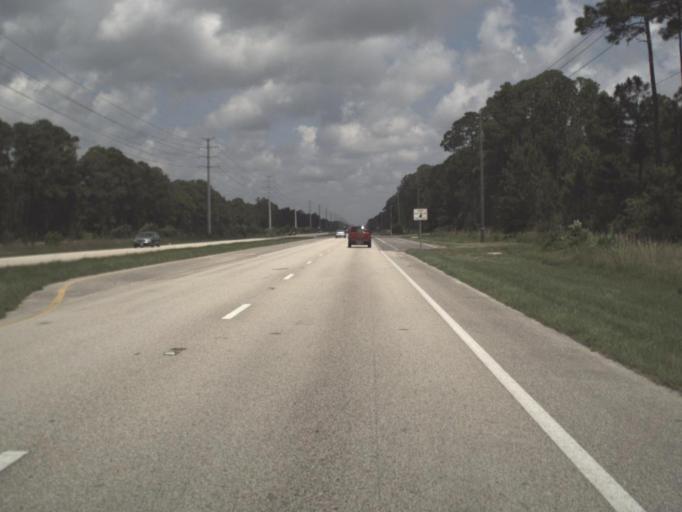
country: US
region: Florida
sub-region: Saint Johns County
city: Villano Beach
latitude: 30.0271
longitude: -81.4051
